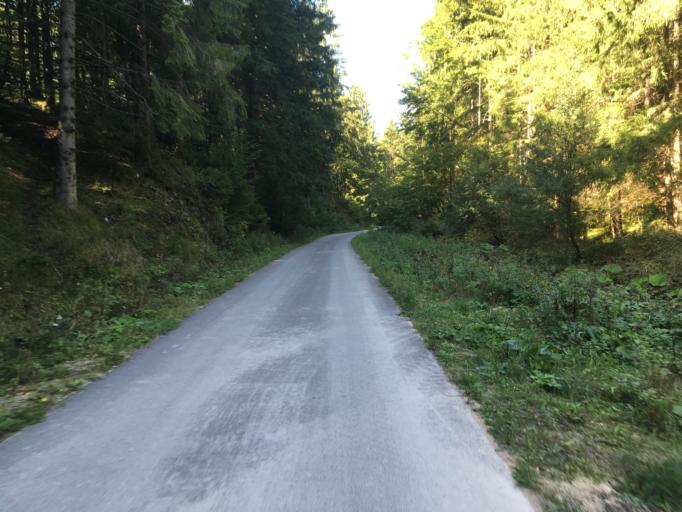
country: SK
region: Trenciansky
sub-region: Okres Povazska Bystrica
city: Povazska Bystrica
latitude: 49.0024
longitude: 18.4703
